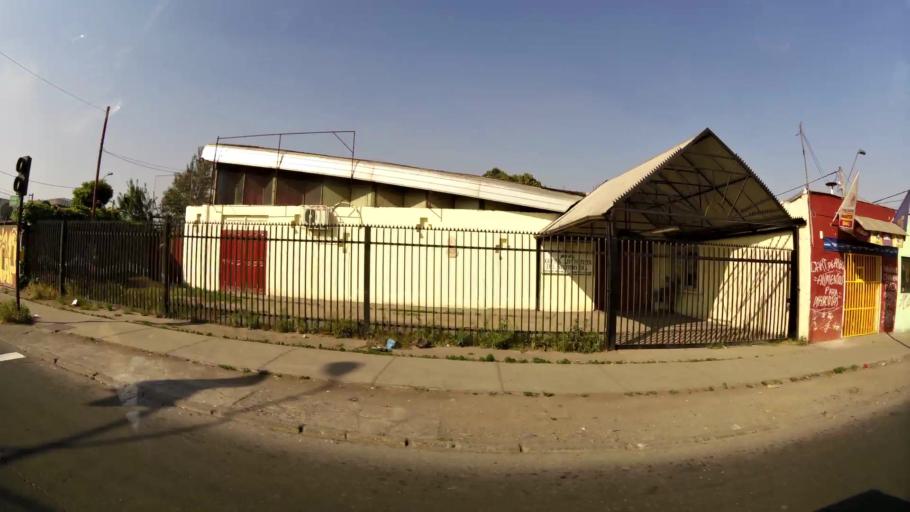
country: CL
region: Santiago Metropolitan
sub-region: Provincia de Santiago
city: Lo Prado
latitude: -33.3783
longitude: -70.6837
